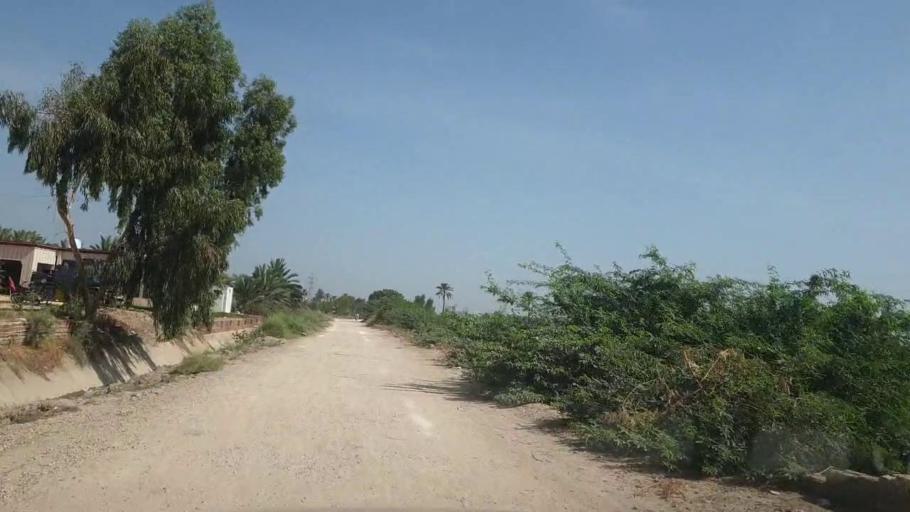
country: PK
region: Sindh
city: Rohri
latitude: 27.6644
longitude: 68.8837
